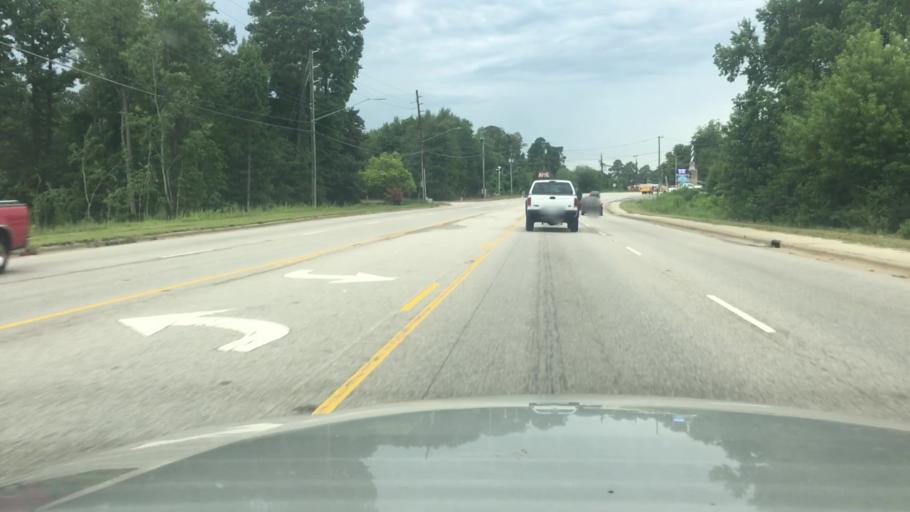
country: US
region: North Carolina
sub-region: Cumberland County
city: Hope Mills
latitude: 34.9920
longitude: -78.9673
